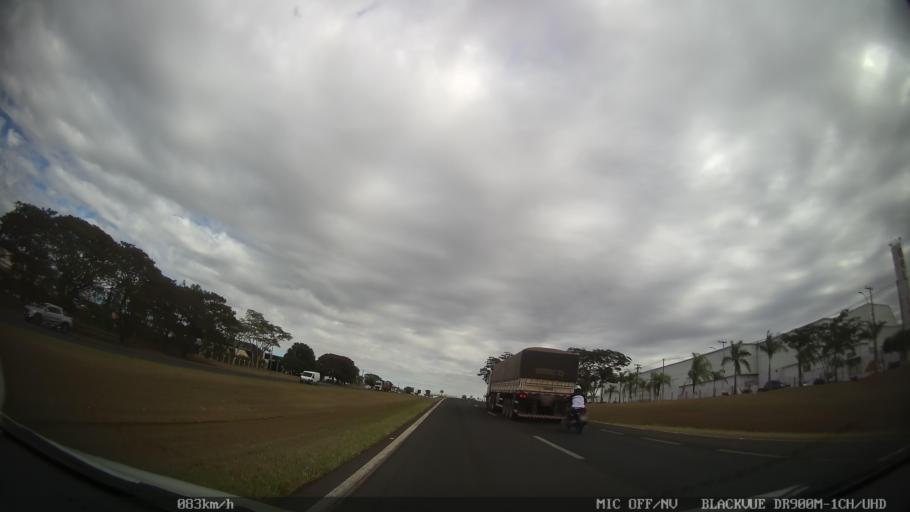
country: BR
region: Sao Paulo
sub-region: Sao Jose Do Rio Preto
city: Sao Jose do Rio Preto
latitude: -20.8116
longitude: -49.4866
